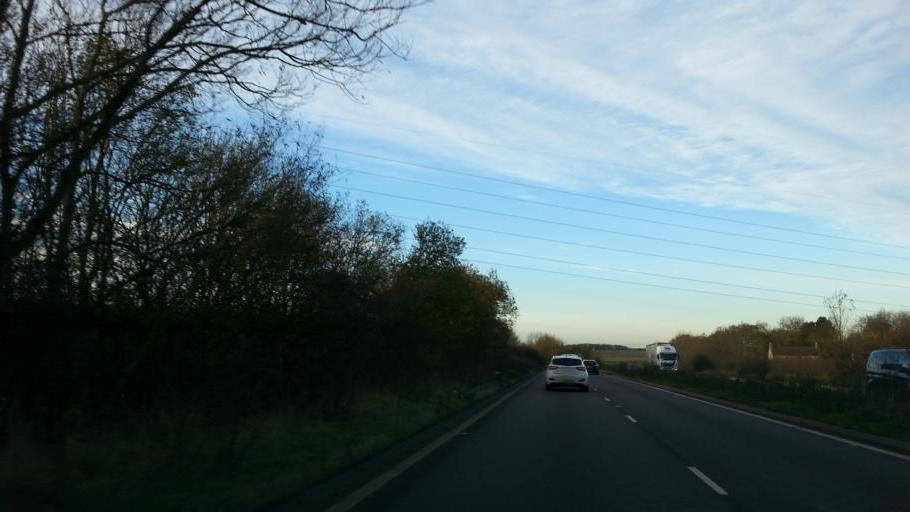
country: GB
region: England
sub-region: Northamptonshire
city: Kettering
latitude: 52.4311
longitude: -0.7338
